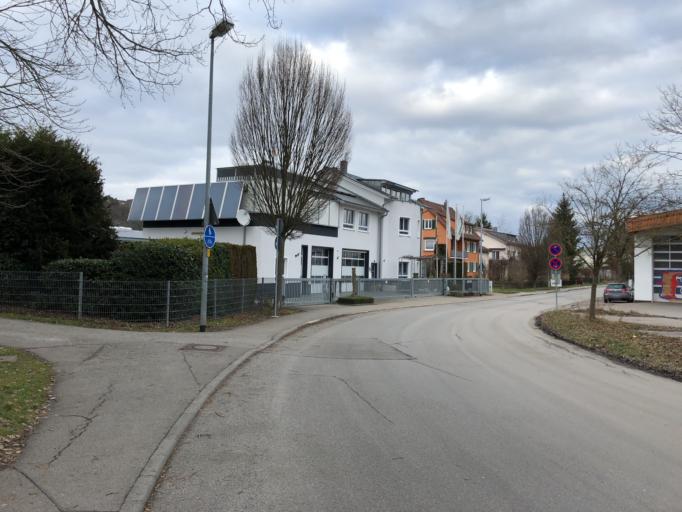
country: DE
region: Baden-Wuerttemberg
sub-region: Tuebingen Region
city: Tuebingen
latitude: 48.5196
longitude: 9.0326
